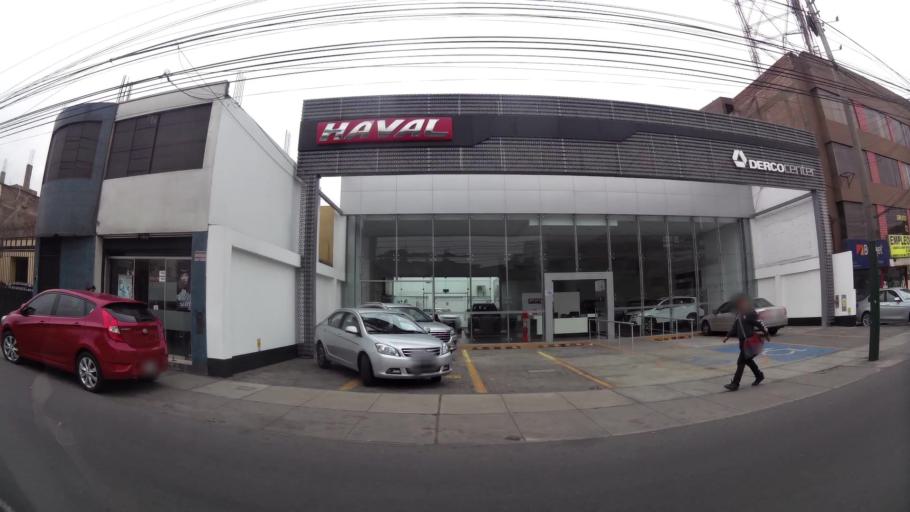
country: PE
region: Lima
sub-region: Lima
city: La Molina
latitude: -12.1101
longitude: -76.9746
